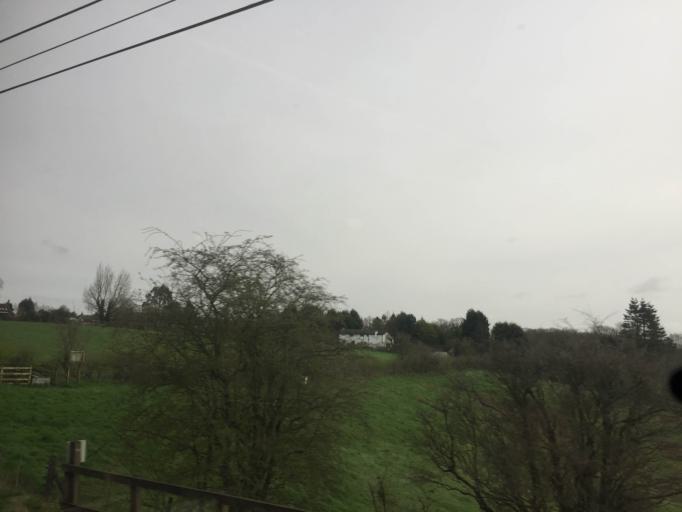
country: GB
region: England
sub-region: Lancashire
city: Coppull
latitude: 53.6329
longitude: -2.6630
